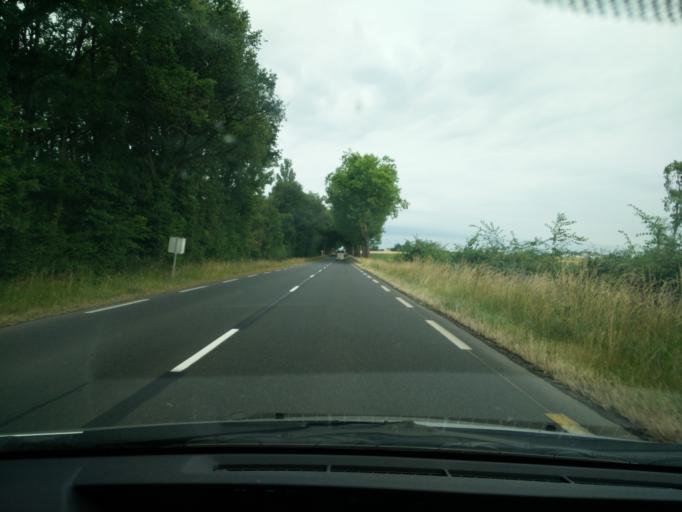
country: FR
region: Pays de la Loire
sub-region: Departement de Maine-et-Loire
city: Saint-Jean
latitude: 47.3088
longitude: -0.3972
